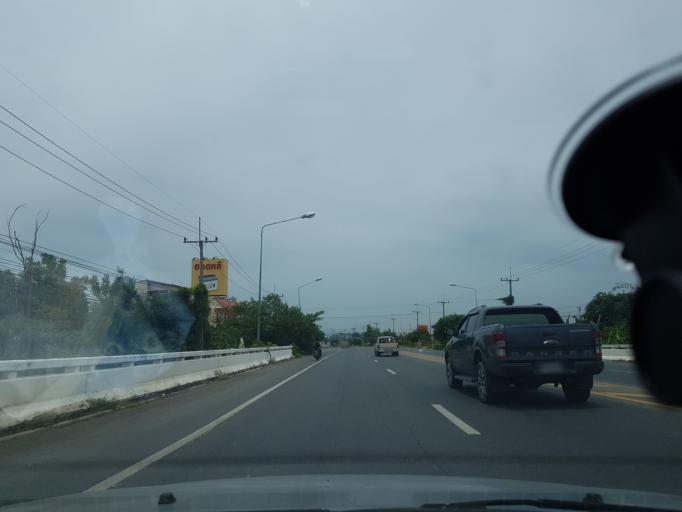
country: TH
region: Lop Buri
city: Lop Buri
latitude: 14.8092
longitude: 100.5907
